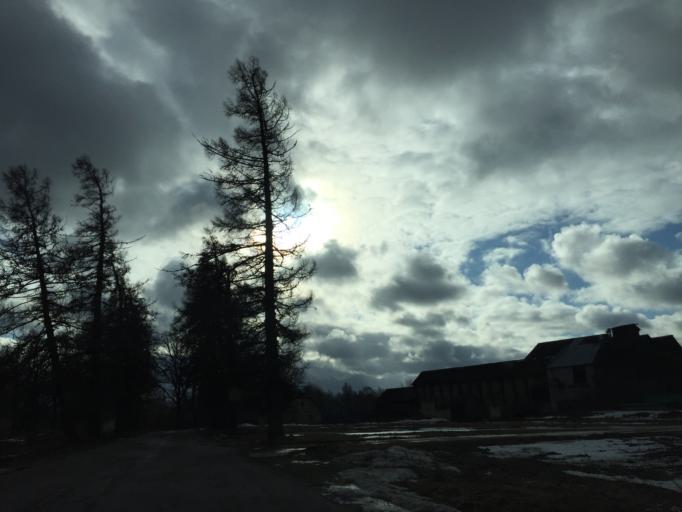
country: LV
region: Aloja
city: Aloja
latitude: 57.7767
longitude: 24.8123
